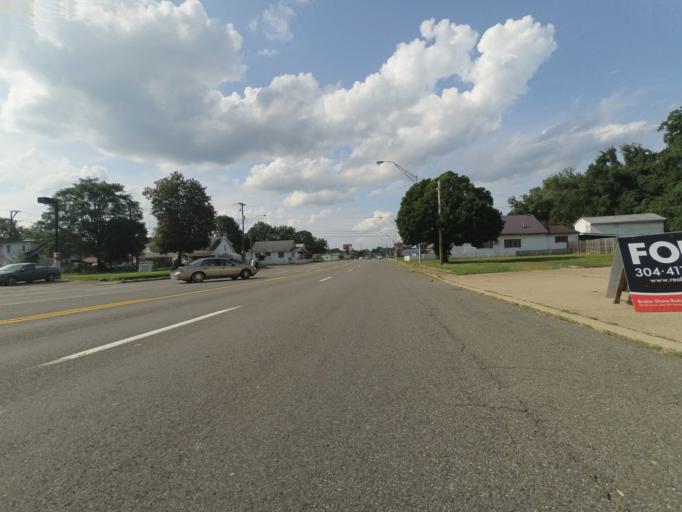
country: US
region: West Virginia
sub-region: Cabell County
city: Huntington
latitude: 38.4248
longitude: -82.3927
